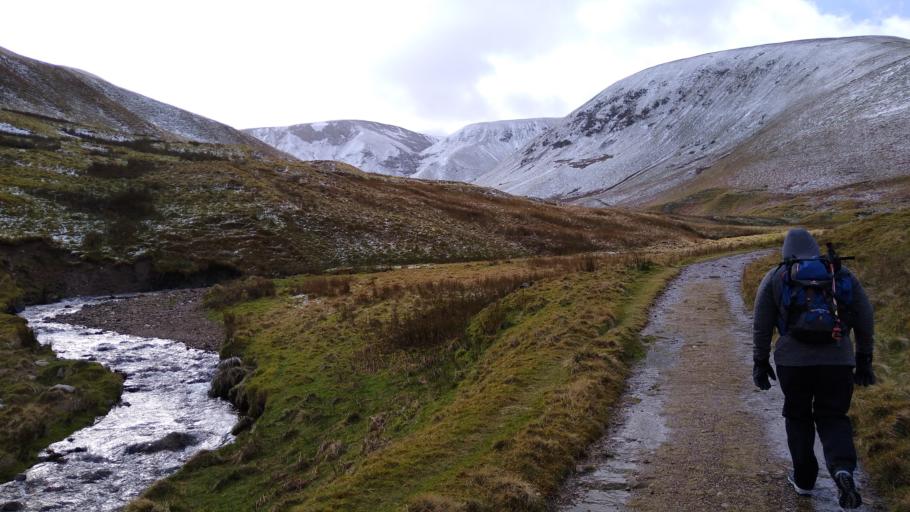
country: GB
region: England
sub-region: Cumbria
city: Keswick
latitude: 54.7090
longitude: -3.0885
